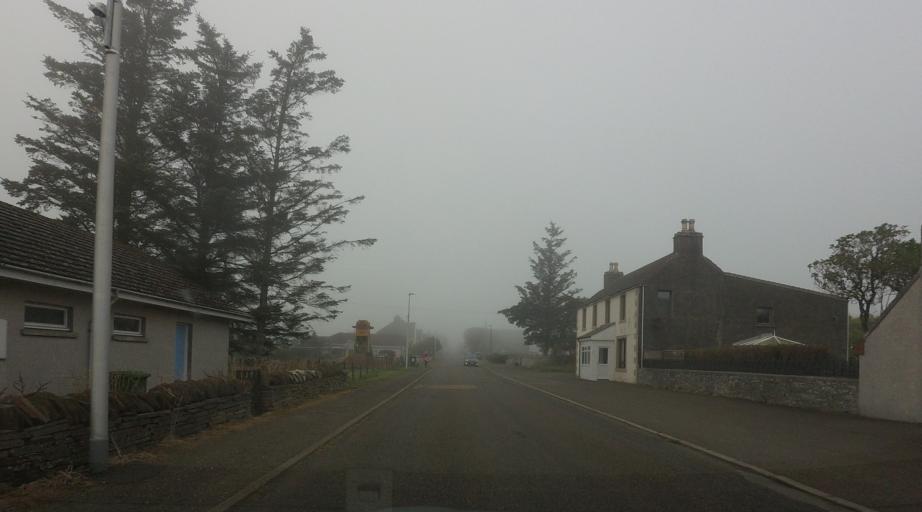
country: GB
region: Scotland
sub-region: Highland
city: Wick
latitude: 58.3049
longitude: -3.2852
